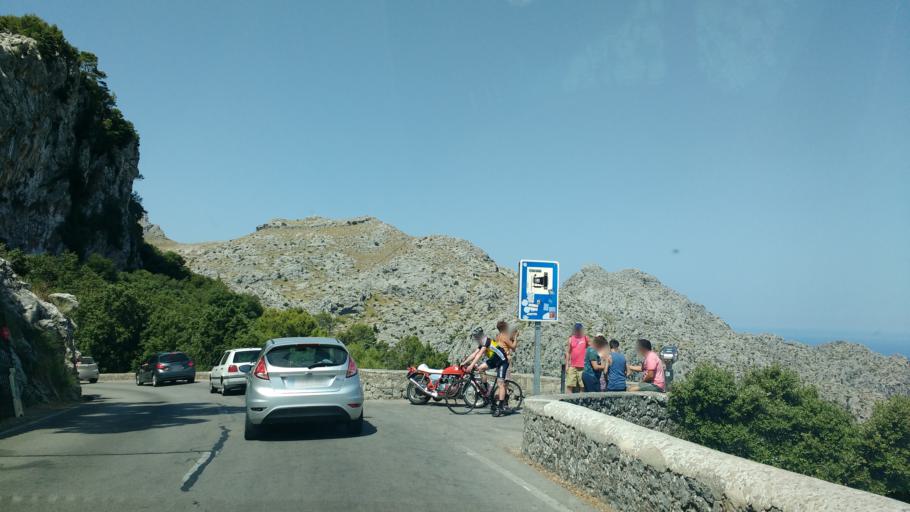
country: ES
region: Balearic Islands
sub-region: Illes Balears
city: Escorca
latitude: 39.8287
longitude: 2.8373
